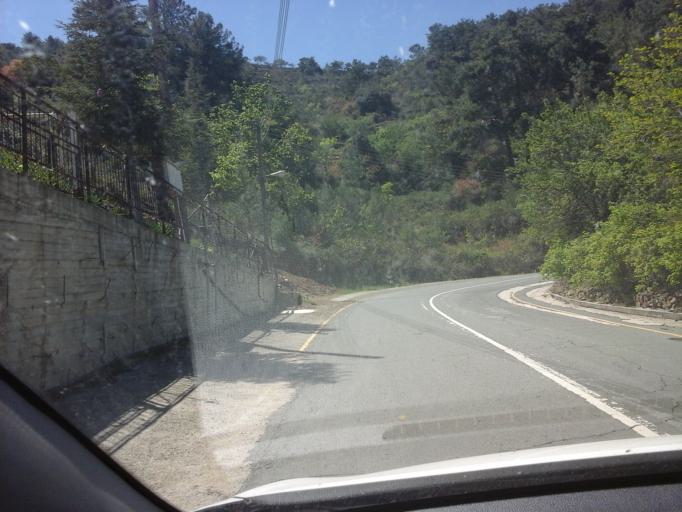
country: CY
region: Lefkosia
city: Kakopetria
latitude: 35.0020
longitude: 32.8021
